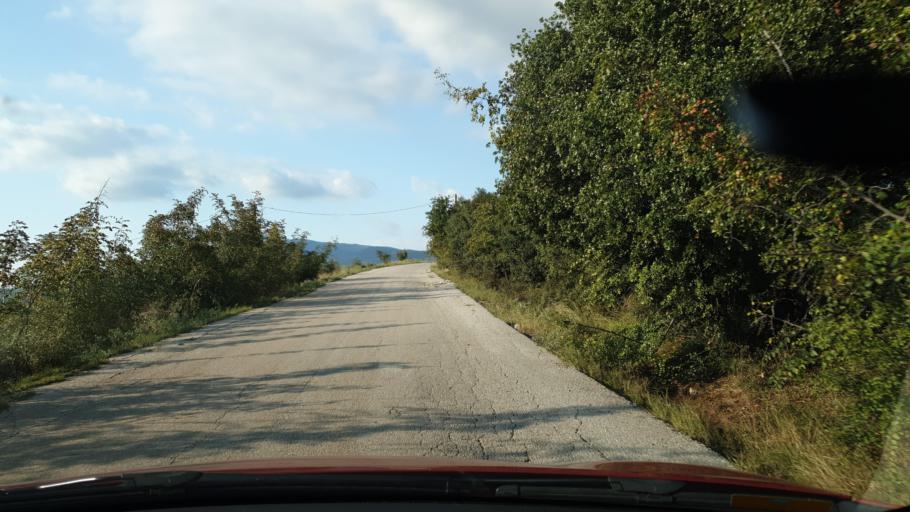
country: GR
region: Central Macedonia
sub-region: Nomos Thessalonikis
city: Vasilika
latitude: 40.5060
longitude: 23.1500
